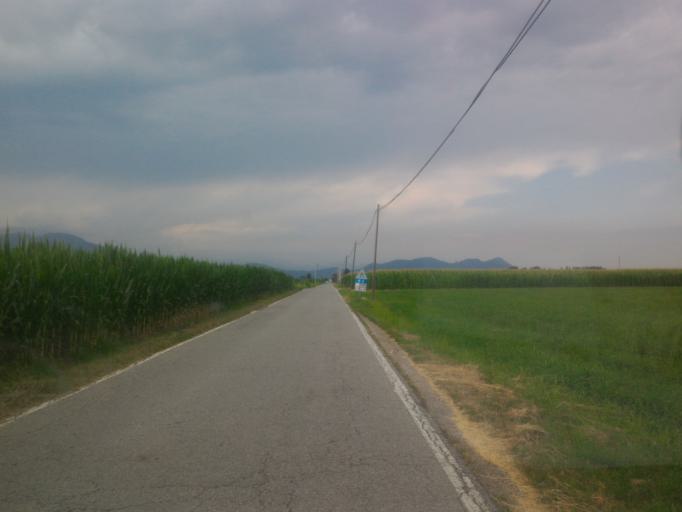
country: IT
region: Piedmont
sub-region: Provincia di Torino
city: Buriasco
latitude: 44.8749
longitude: 7.4023
